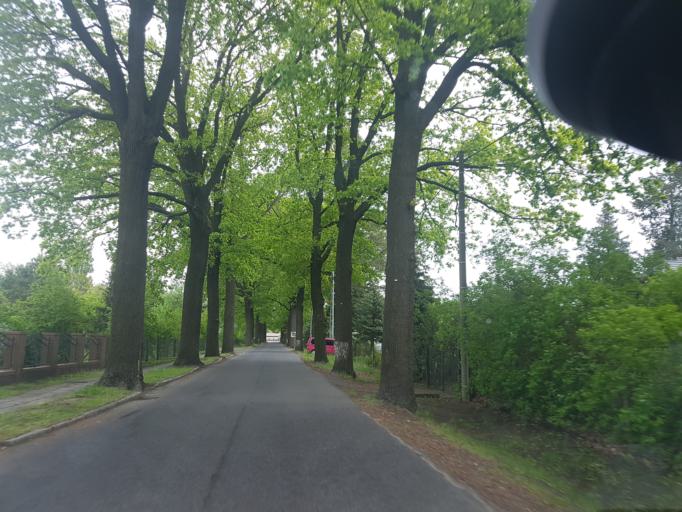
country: DE
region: Brandenburg
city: Neupetershain
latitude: 51.6081
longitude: 14.1587
